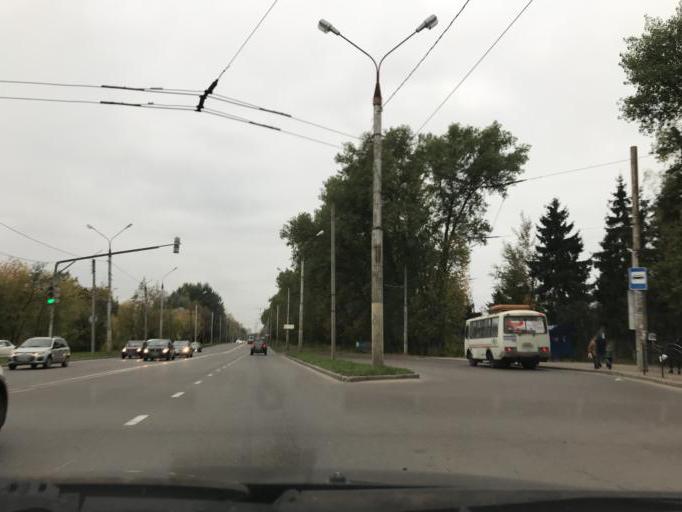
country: RU
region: Kaluga
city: Kaluga
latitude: 54.6037
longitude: 36.2651
